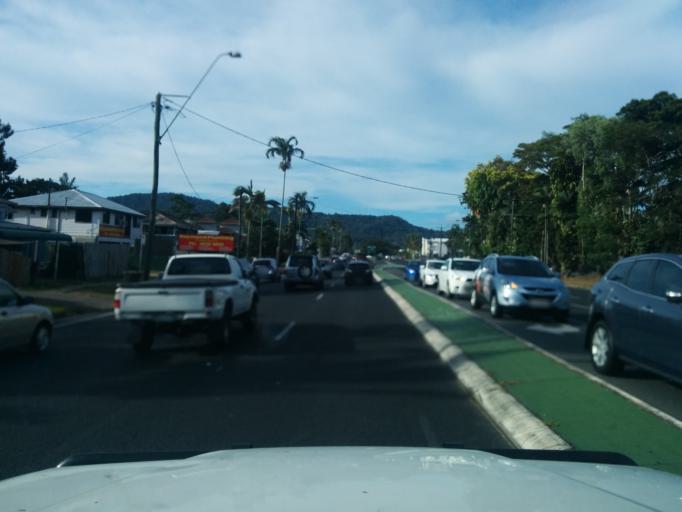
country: AU
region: Queensland
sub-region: Cairns
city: Cairns
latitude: -16.9225
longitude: 145.7400
